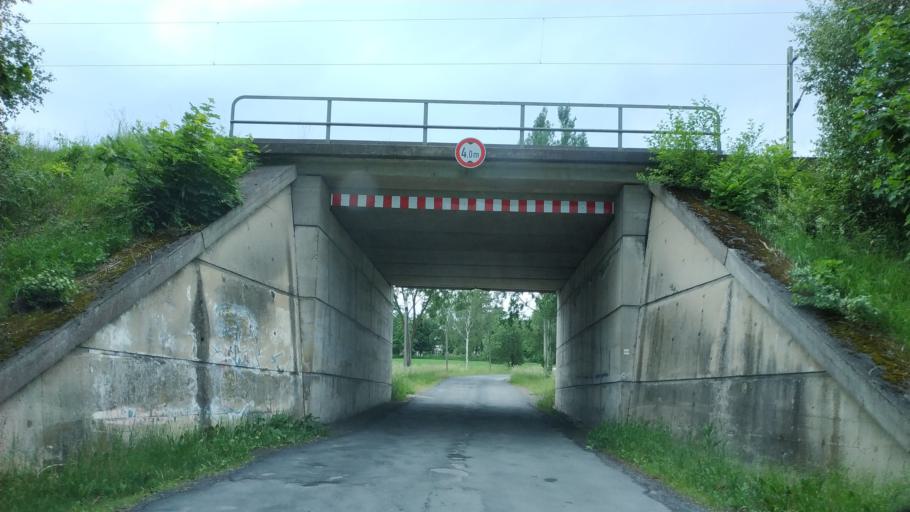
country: DE
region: Saxony
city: Syrau
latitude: 50.5344
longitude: 12.1166
